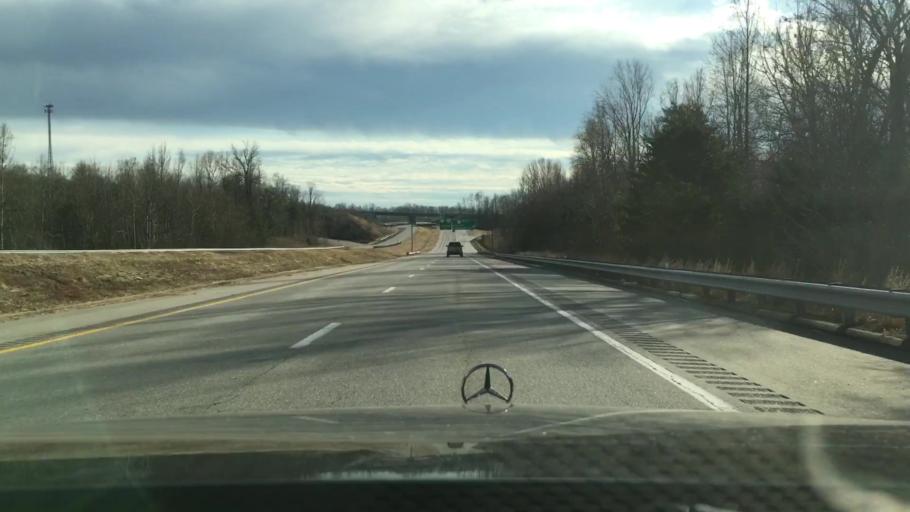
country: US
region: Virginia
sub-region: City of Danville
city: Danville
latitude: 36.6229
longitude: -79.3651
